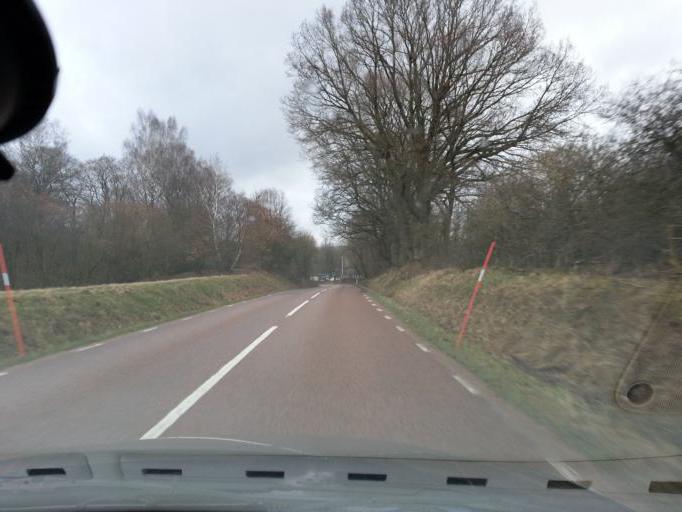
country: SE
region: Skane
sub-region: Astorps Kommun
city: Kvidinge
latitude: 56.1102
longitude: 13.0944
